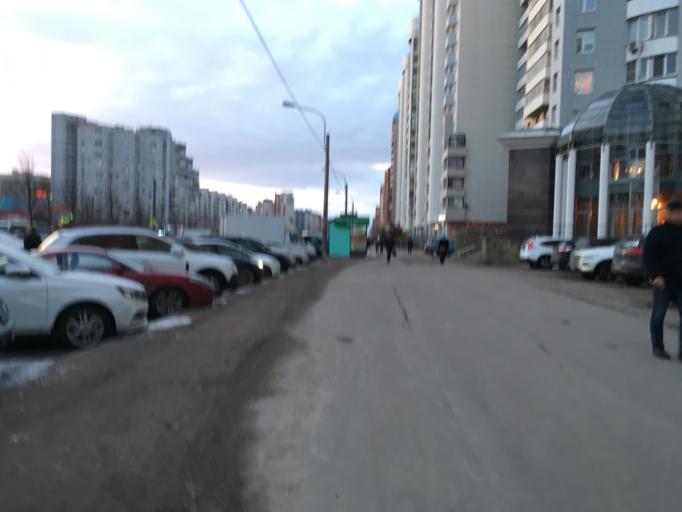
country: RU
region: St.-Petersburg
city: Komendantsky aerodrom
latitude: 60.0124
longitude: 30.2551
